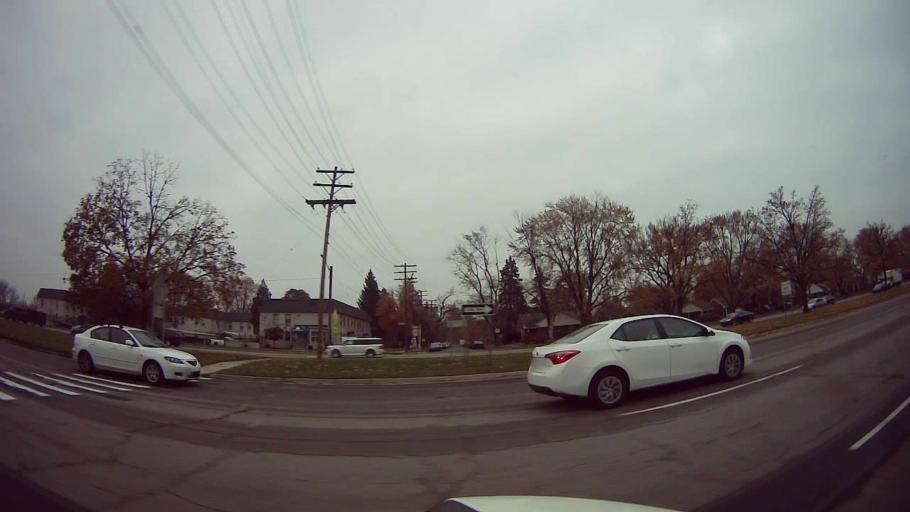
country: US
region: Michigan
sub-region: Wayne County
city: Redford
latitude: 42.4352
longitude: -83.2785
